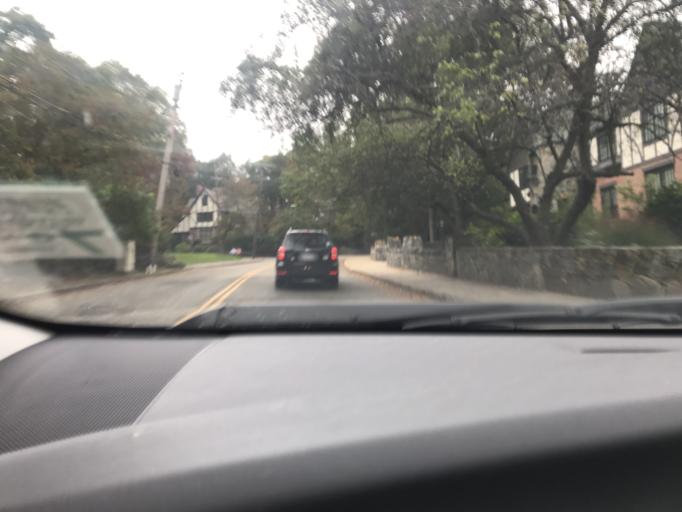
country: US
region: Massachusetts
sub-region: Middlesex County
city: Newton
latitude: 42.3381
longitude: -71.2136
